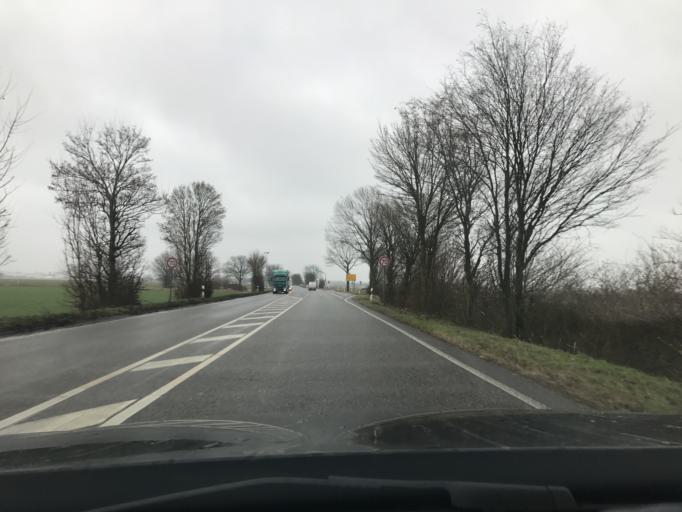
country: DE
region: North Rhine-Westphalia
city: Tonisvorst
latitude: 51.3615
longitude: 6.5013
